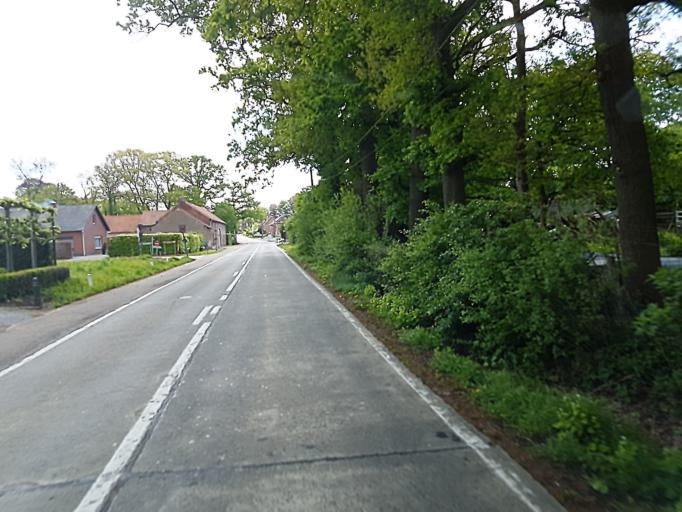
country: BE
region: Flanders
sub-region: Provincie Vlaams-Brabant
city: Diest
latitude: 51.0137
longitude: 5.0220
